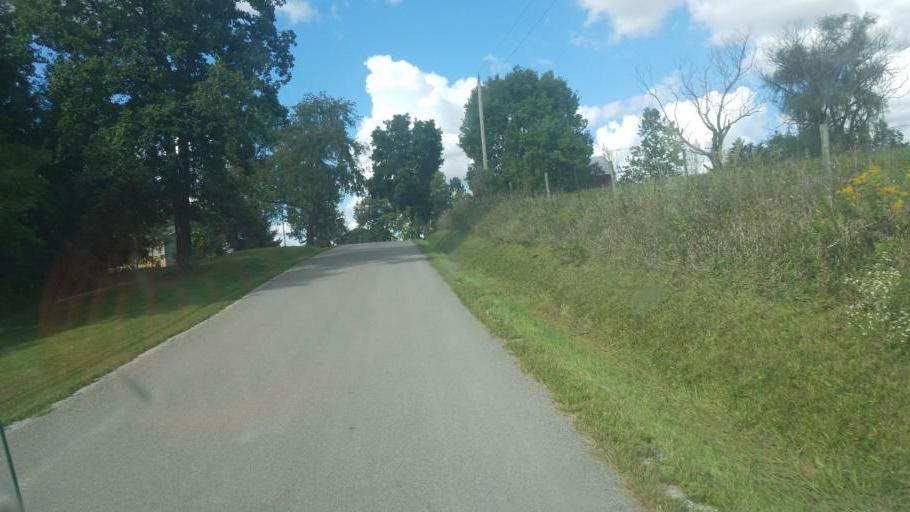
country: US
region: Ohio
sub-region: Hardin County
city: Kenton
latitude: 40.5430
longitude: -83.5438
